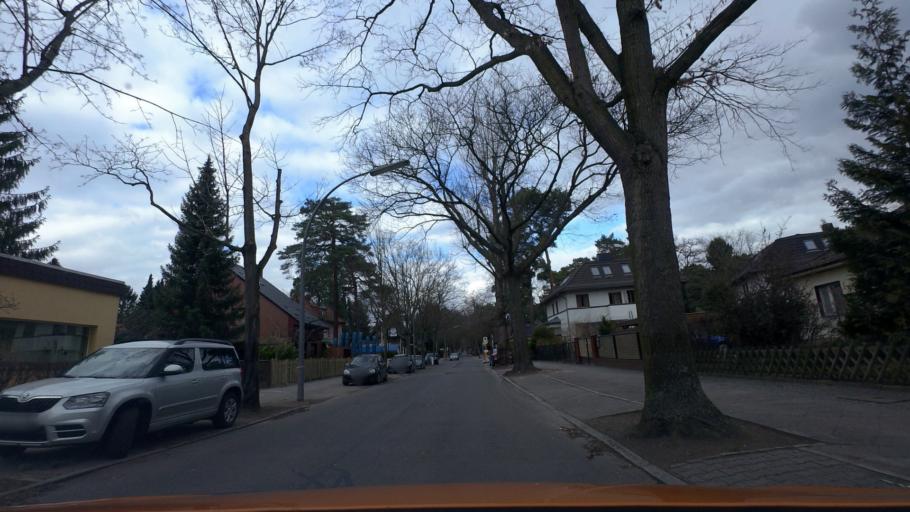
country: DE
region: Berlin
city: Konradshohe
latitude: 52.5866
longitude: 13.2264
